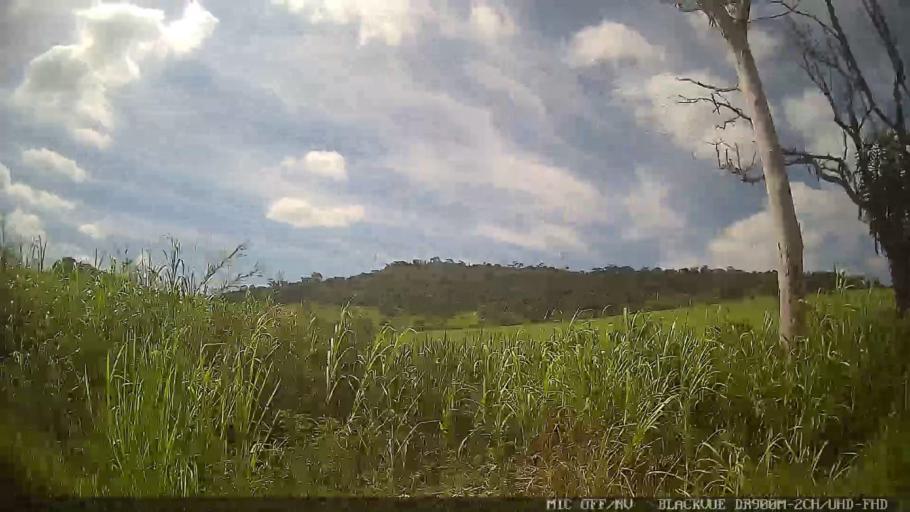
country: BR
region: Sao Paulo
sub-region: Braganca Paulista
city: Braganca Paulista
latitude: -22.9705
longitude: -46.6328
